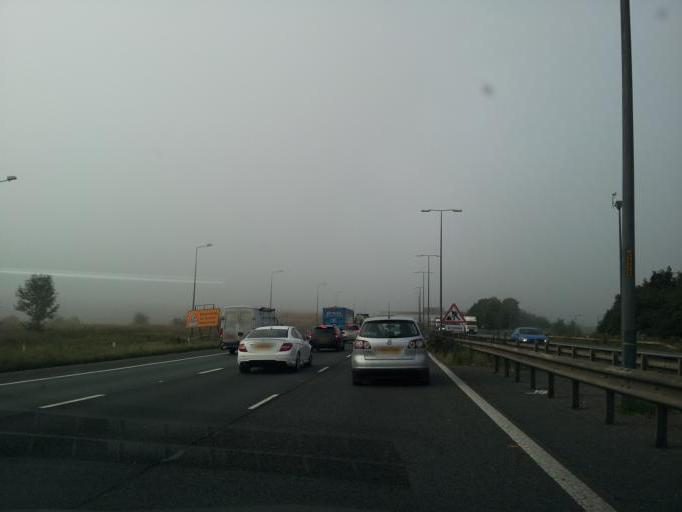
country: GB
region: England
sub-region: Borough of Rochdale
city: Milnrow
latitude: 53.6019
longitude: -2.1104
